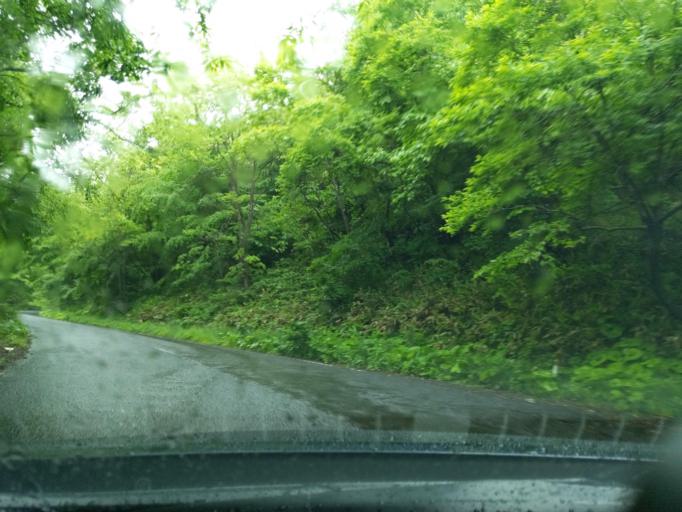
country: JP
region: Fukushima
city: Funehikimachi-funehiki
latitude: 37.6131
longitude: 140.6844
